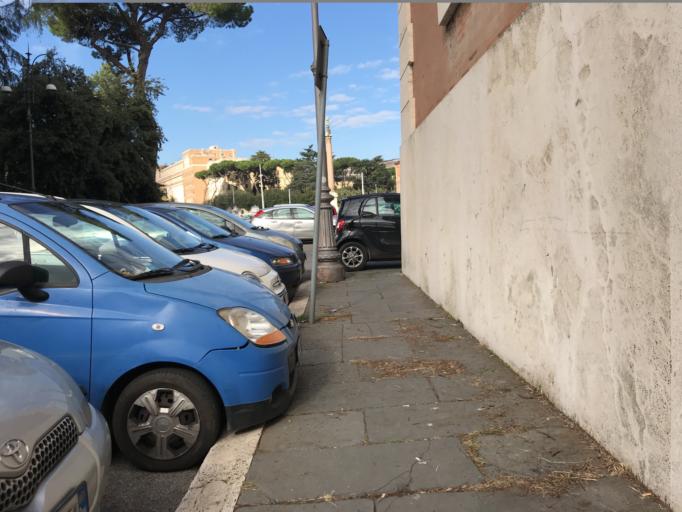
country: IT
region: Latium
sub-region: Citta metropolitana di Roma Capitale
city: Rome
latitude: 41.9015
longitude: 12.5202
